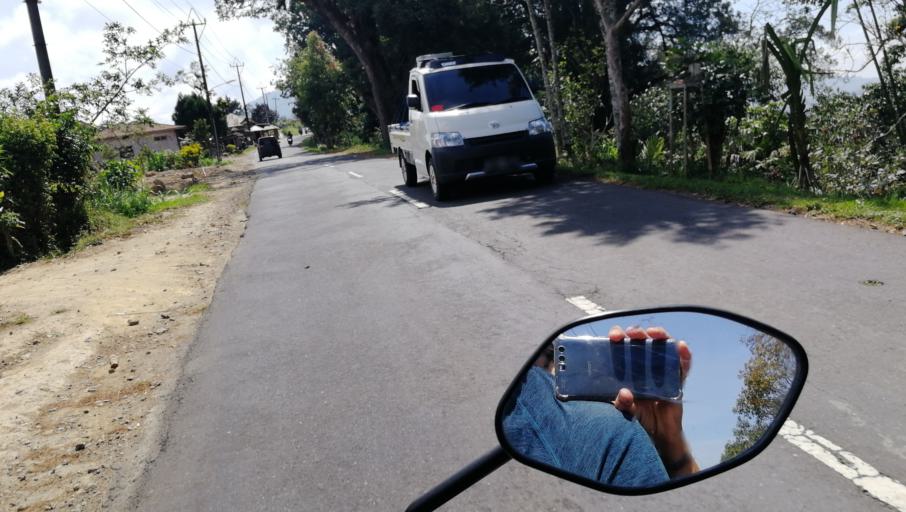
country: ID
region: Bali
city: Munduk
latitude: -8.2367
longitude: 115.1253
